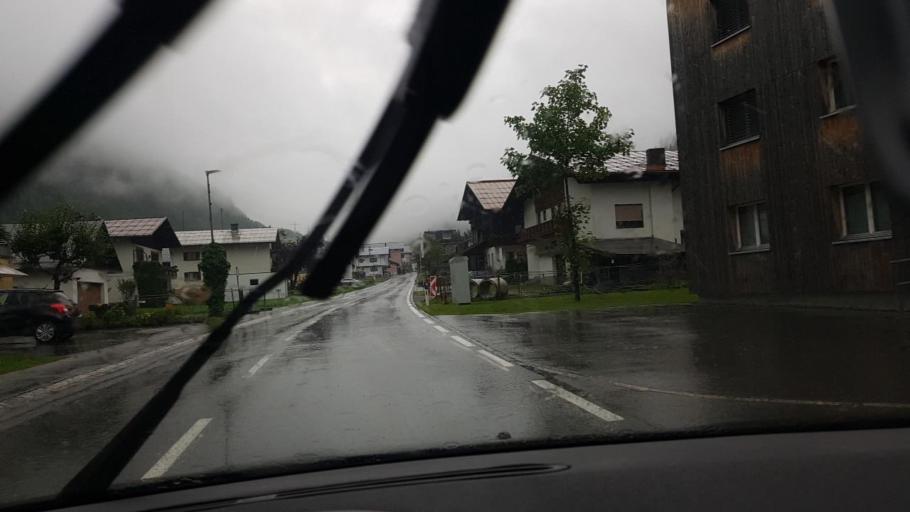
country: AT
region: Vorarlberg
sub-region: Politischer Bezirk Bludenz
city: Klosterle
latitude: 47.1315
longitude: 10.0854
